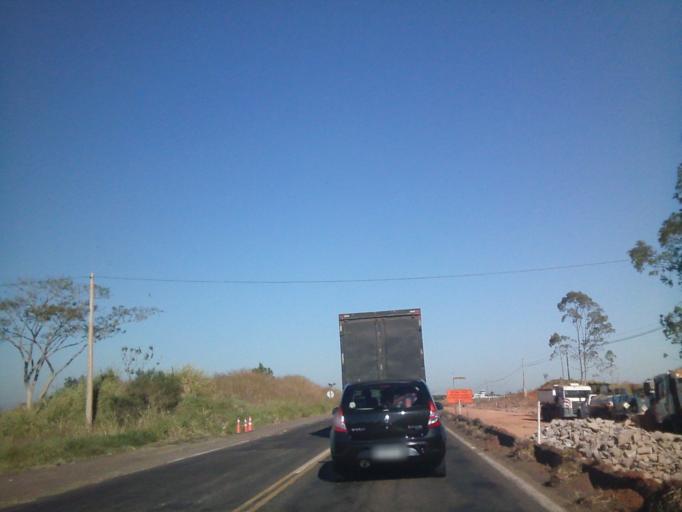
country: BR
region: Sao Paulo
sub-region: Presidente Prudente
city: Presidente Prudente
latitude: -22.1738
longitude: -51.4064
